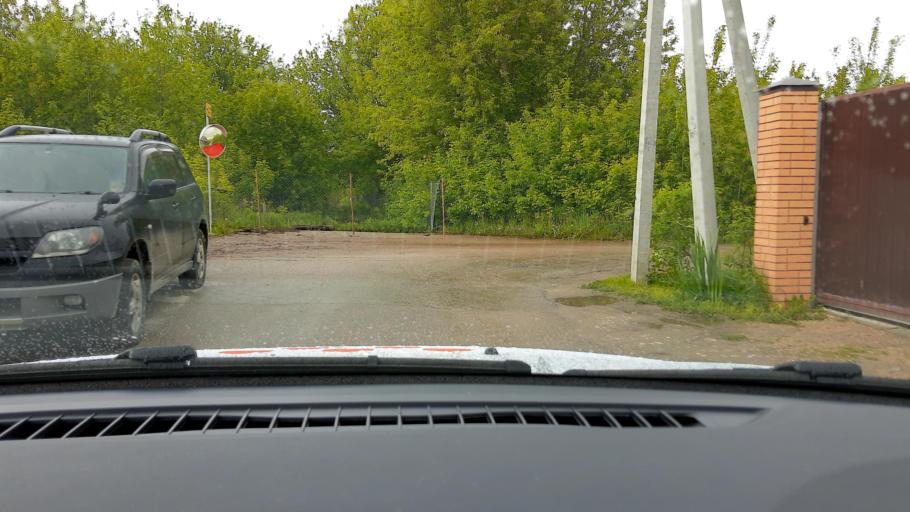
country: RU
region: Nizjnij Novgorod
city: Afonino
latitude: 56.2714
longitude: 44.0986
